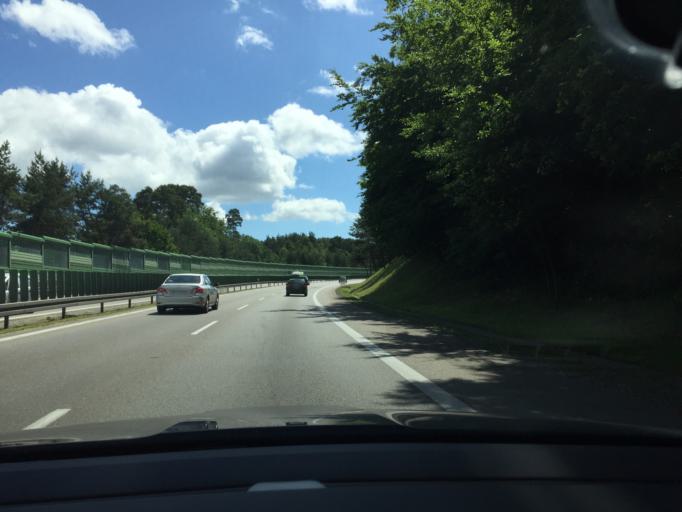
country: PL
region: Pomeranian Voivodeship
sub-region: Gdynia
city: Pogorze
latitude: 54.5273
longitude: 18.4570
